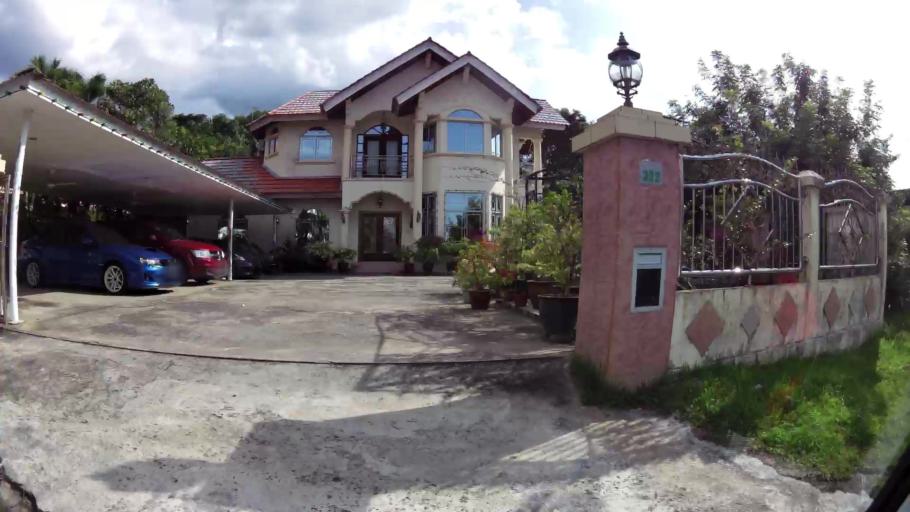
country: BN
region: Brunei and Muara
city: Bandar Seri Begawan
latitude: 4.9562
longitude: 114.9718
